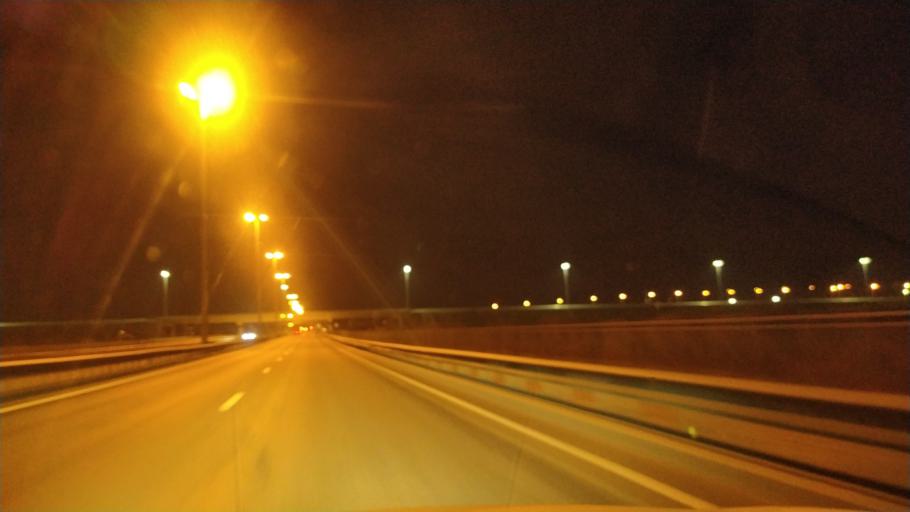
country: RU
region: St.-Petersburg
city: Pushkin
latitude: 59.7600
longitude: 30.3949
